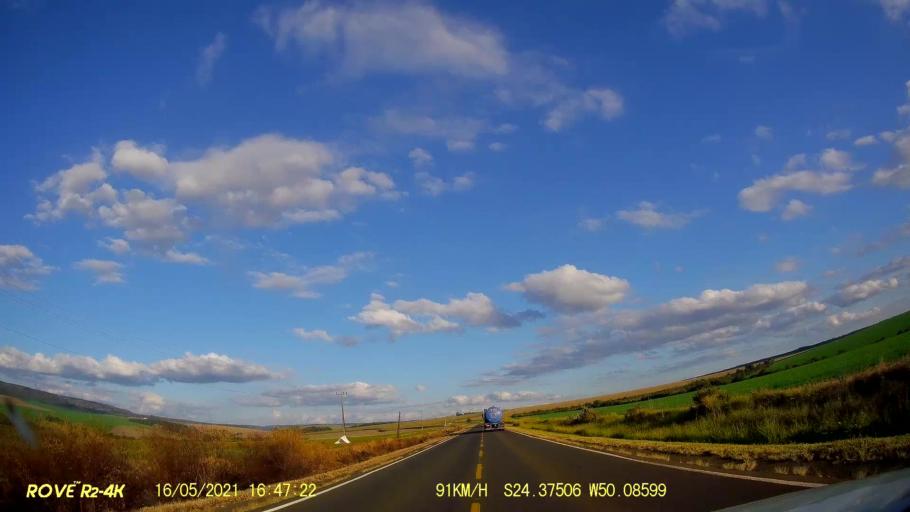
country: BR
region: Parana
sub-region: Pirai Do Sul
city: Pirai do Sul
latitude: -24.3753
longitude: -50.0858
